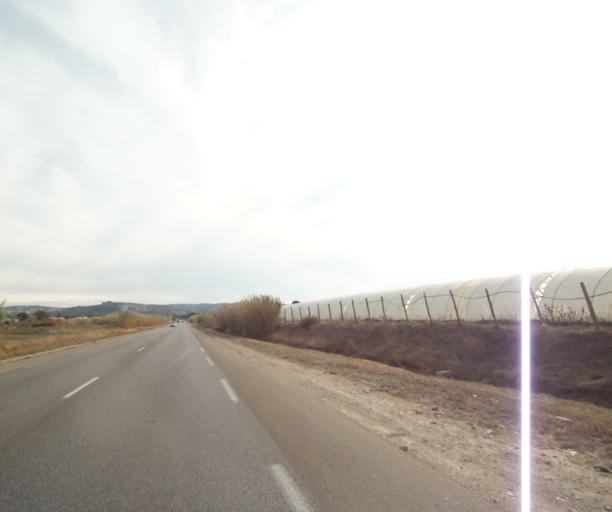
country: FR
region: Provence-Alpes-Cote d'Azur
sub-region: Departement des Bouches-du-Rhone
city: Gignac-la-Nerthe
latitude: 43.3900
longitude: 5.2101
